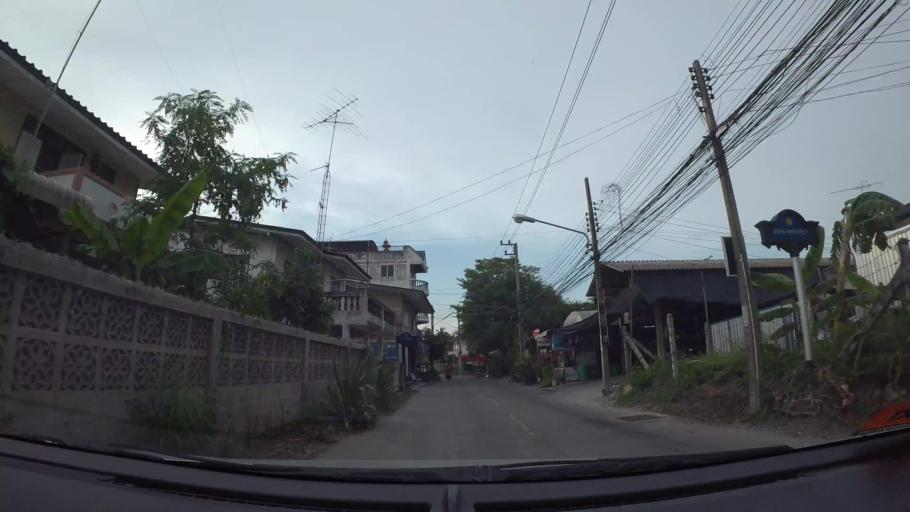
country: TH
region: Chon Buri
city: Chon Buri
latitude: 13.3417
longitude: 100.9819
